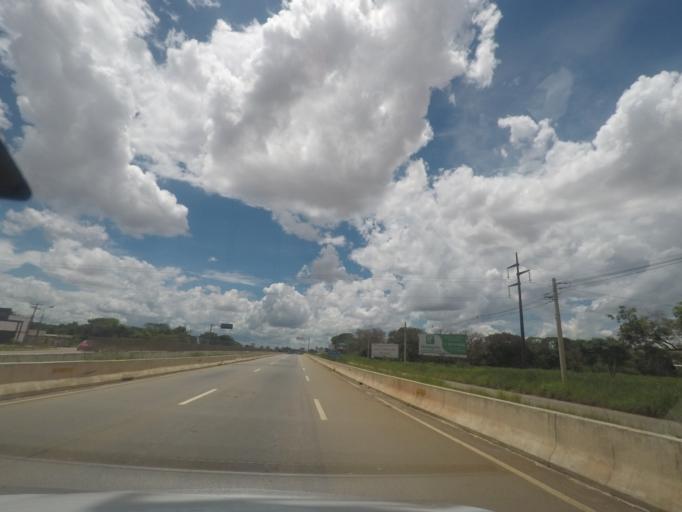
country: BR
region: Goias
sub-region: Goiania
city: Goiania
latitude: -16.7032
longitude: -49.3401
